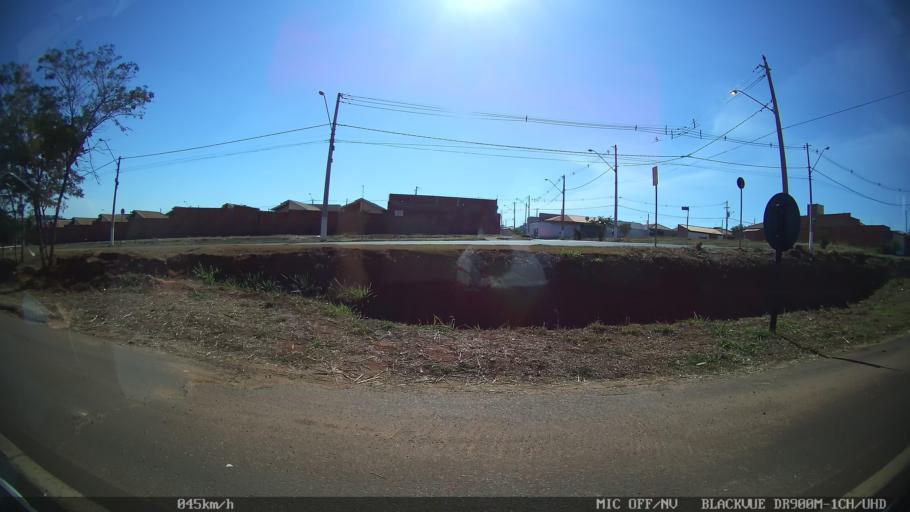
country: BR
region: Sao Paulo
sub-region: Olimpia
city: Olimpia
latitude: -20.7347
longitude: -48.8751
